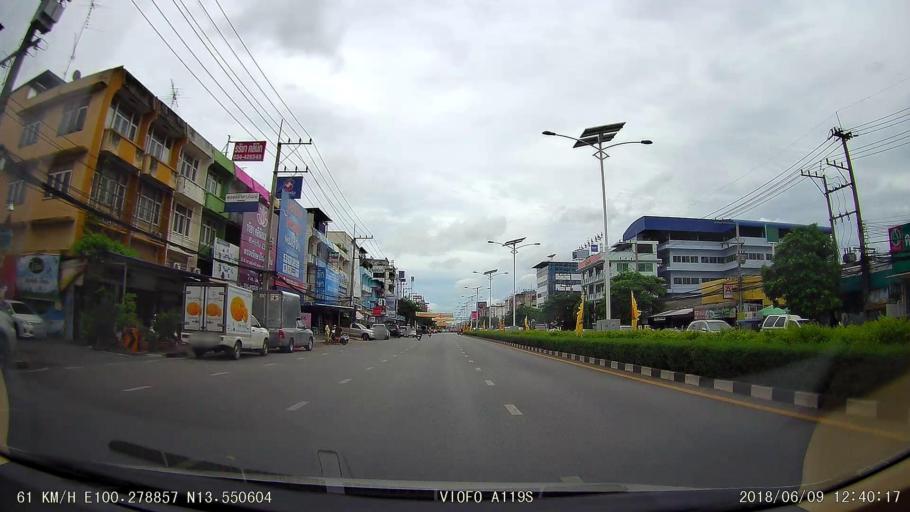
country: TH
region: Samut Sakhon
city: Samut Sakhon
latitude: 13.5505
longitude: 100.2786
